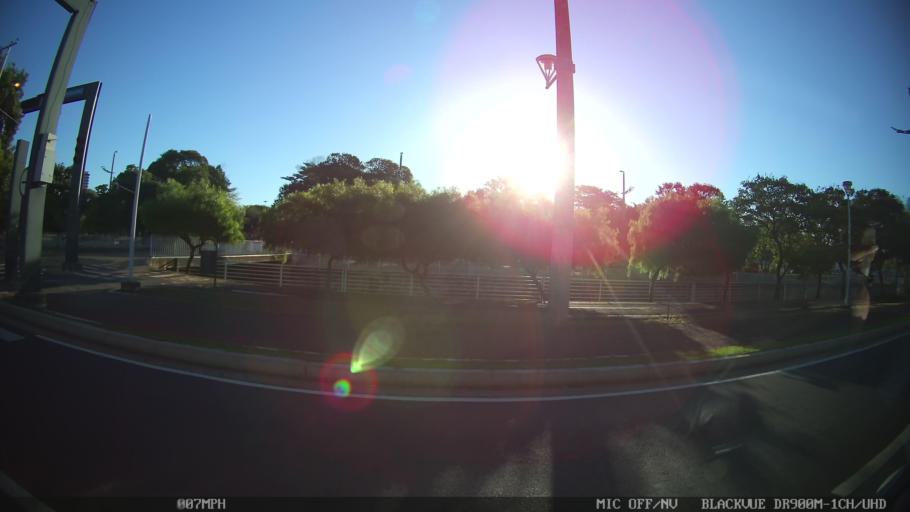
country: BR
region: Sao Paulo
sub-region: Sao Jose Do Rio Preto
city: Sao Jose do Rio Preto
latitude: -20.7992
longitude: -49.3771
